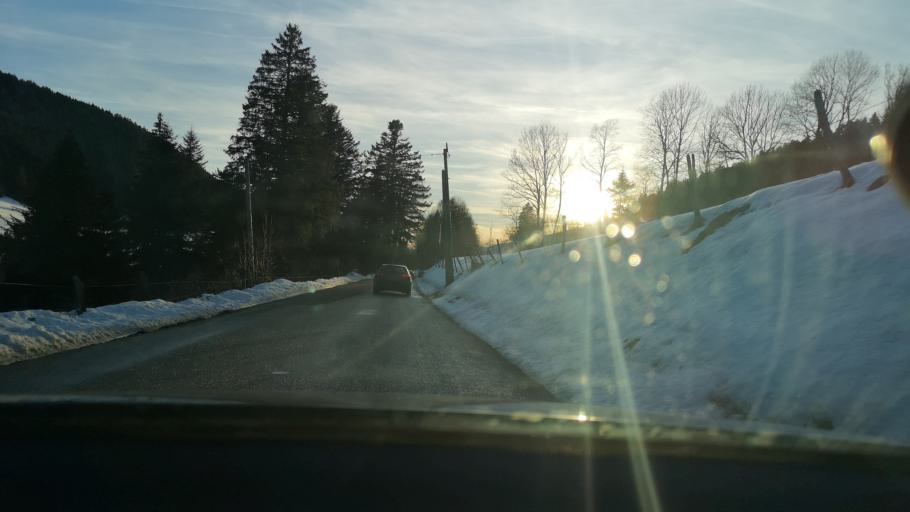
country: FR
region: Franche-Comte
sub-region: Departement du Doubs
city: La Cluse-et-Mijoux
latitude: 46.9326
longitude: 6.4177
